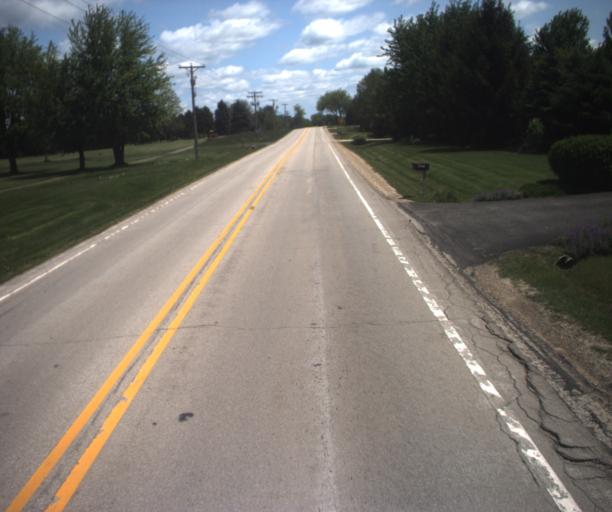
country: US
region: Illinois
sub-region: Kane County
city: Batavia
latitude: 41.8622
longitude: -88.3819
